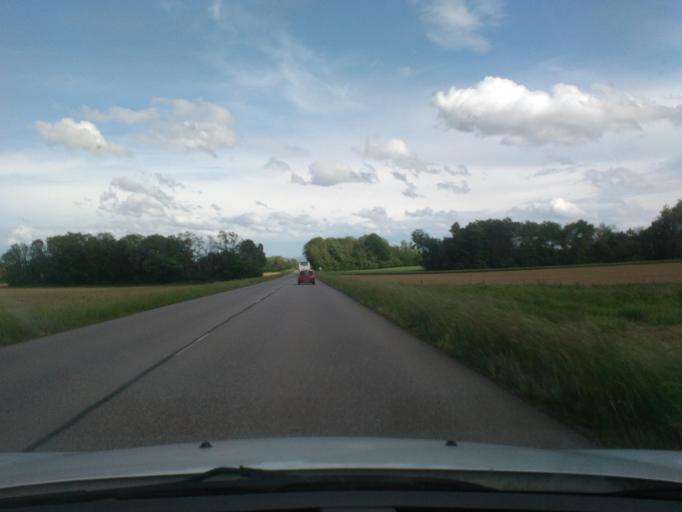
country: FR
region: Lorraine
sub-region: Departement de Meurthe-et-Moselle
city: Baccarat
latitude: 48.5528
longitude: 6.7093
